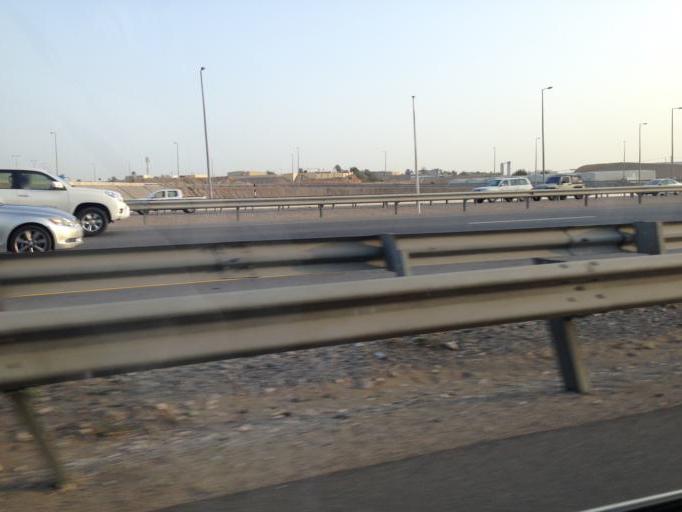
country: OM
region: Muhafazat Masqat
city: Bawshar
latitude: 23.5609
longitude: 58.3394
